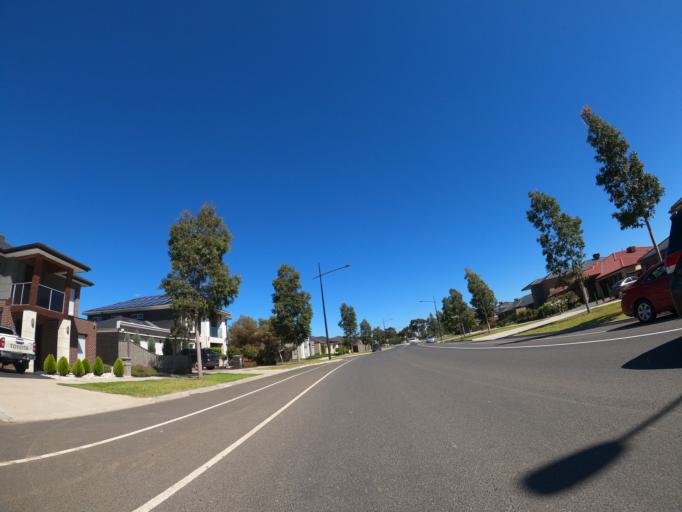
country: AU
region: Victoria
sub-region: Hume
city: Craigieburn
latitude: -37.5317
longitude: 144.9069
